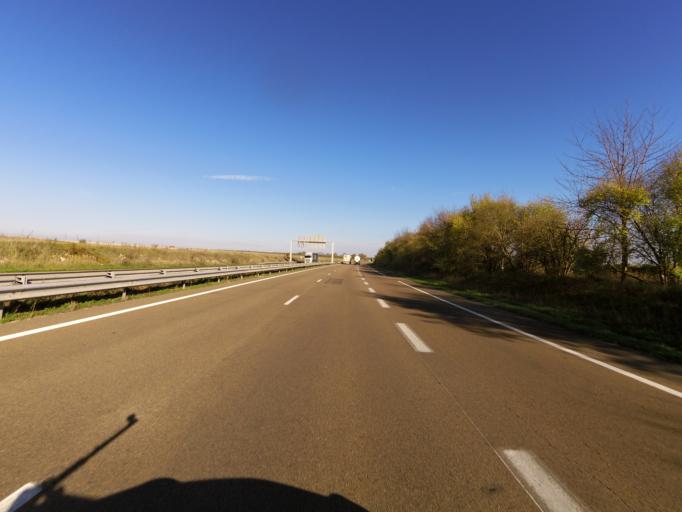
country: FR
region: Champagne-Ardenne
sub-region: Departement de la Marne
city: Fagnieres
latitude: 48.9732
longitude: 4.2844
